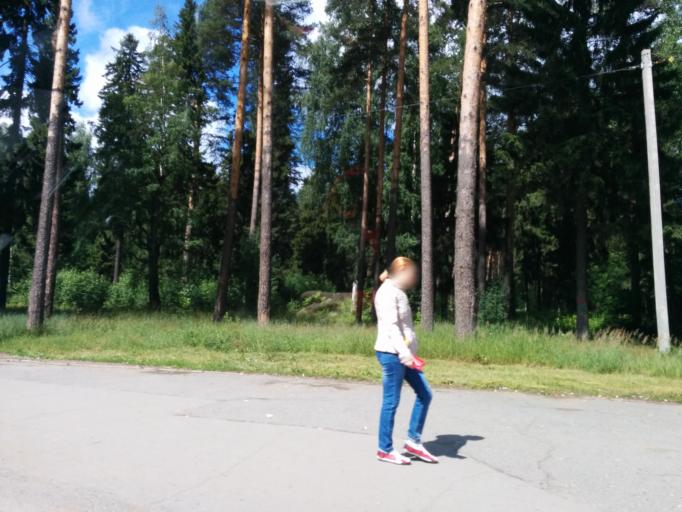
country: RU
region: Perm
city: Kondratovo
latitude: 58.0344
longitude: 56.0205
